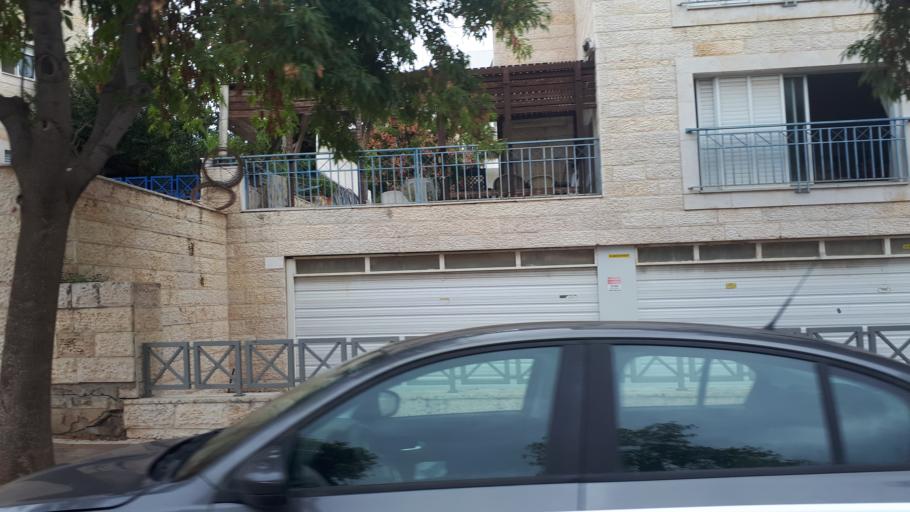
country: IL
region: Central District
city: Modiin
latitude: 31.9038
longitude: 35.0085
